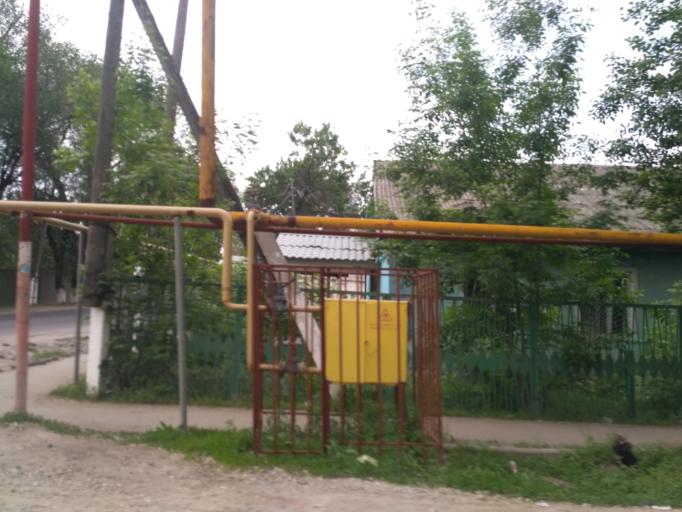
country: KZ
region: Almaty Oblysy
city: Burunday
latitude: 43.4600
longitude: 76.7260
